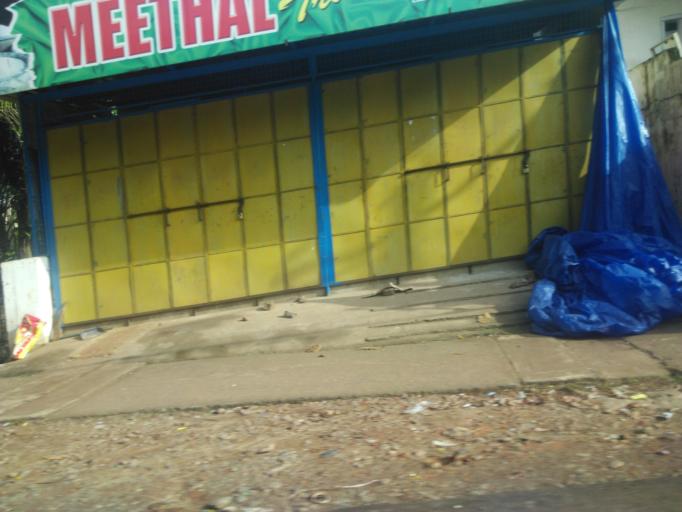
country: IN
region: Kerala
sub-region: Kozhikode
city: Kunnamangalam
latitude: 11.2949
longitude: 75.8290
